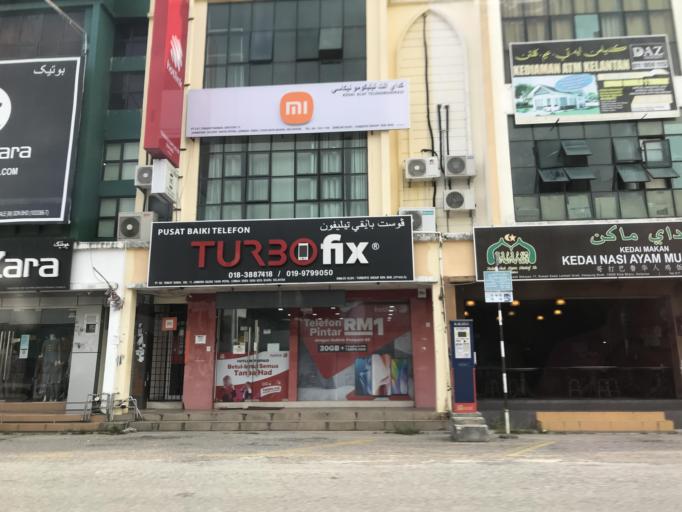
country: MY
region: Kelantan
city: Kota Bharu
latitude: 6.1138
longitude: 102.2310
